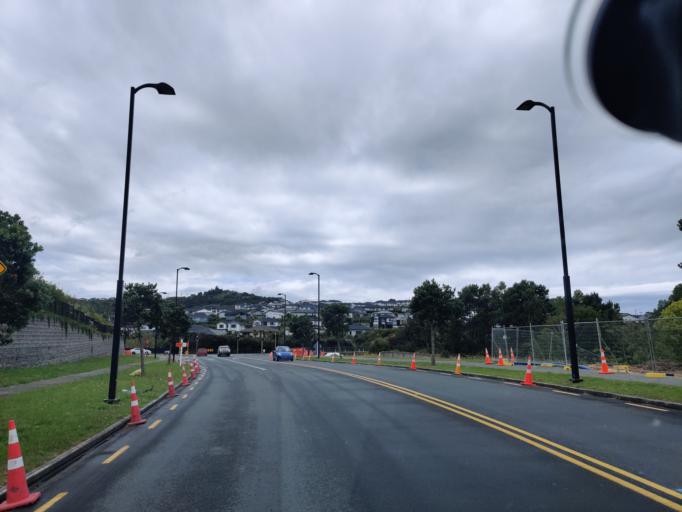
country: NZ
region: Auckland
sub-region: Auckland
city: Rothesay Bay
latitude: -36.5903
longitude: 174.6715
